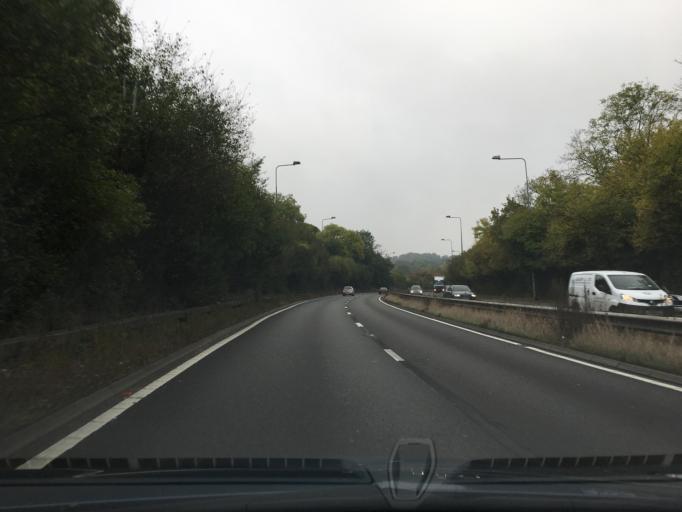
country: GB
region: England
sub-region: Surrey
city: Guildford
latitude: 51.2362
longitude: -0.6018
